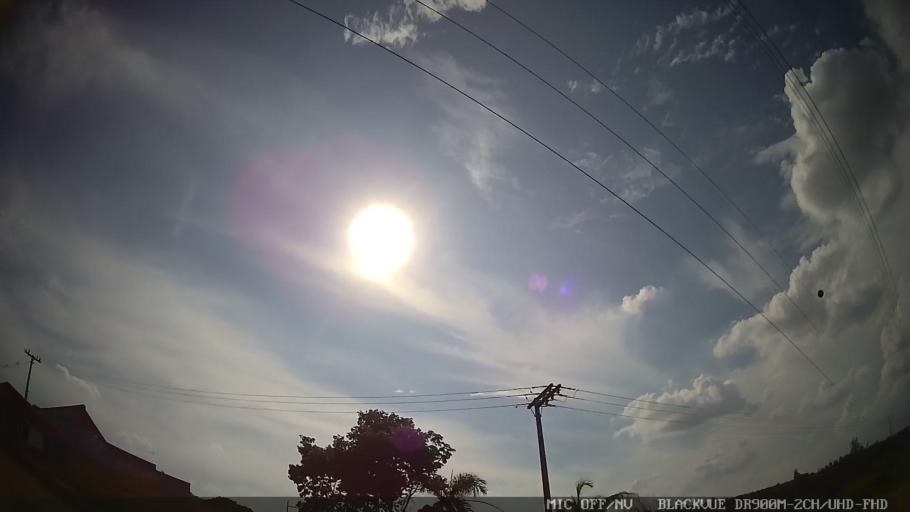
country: BR
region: Sao Paulo
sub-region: Braganca Paulista
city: Braganca Paulista
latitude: -22.9440
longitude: -46.5565
